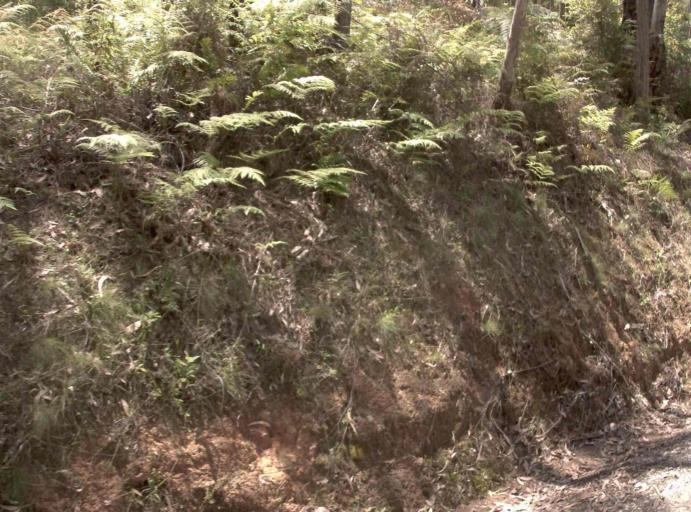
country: AU
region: New South Wales
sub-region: Bombala
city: Bombala
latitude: -37.4875
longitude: 148.9279
